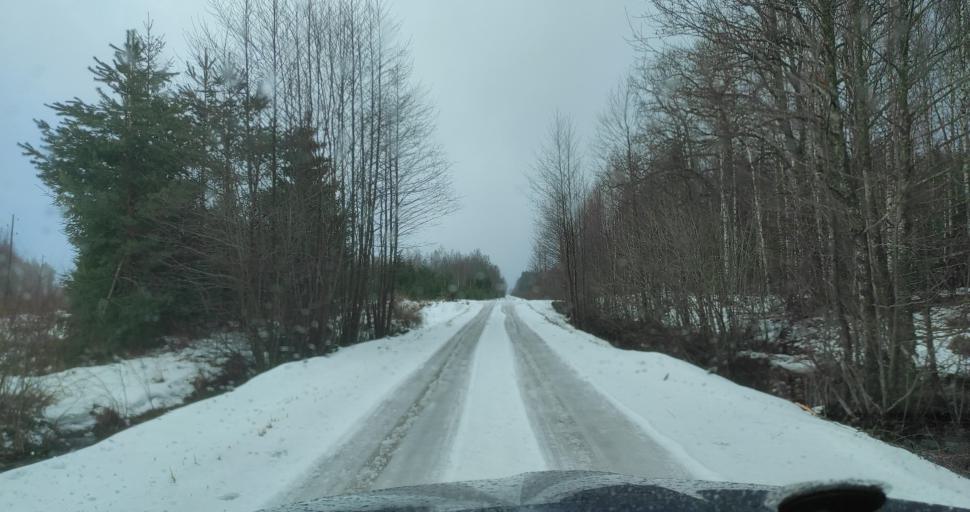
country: LV
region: Dundaga
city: Dundaga
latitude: 57.3867
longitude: 22.1416
